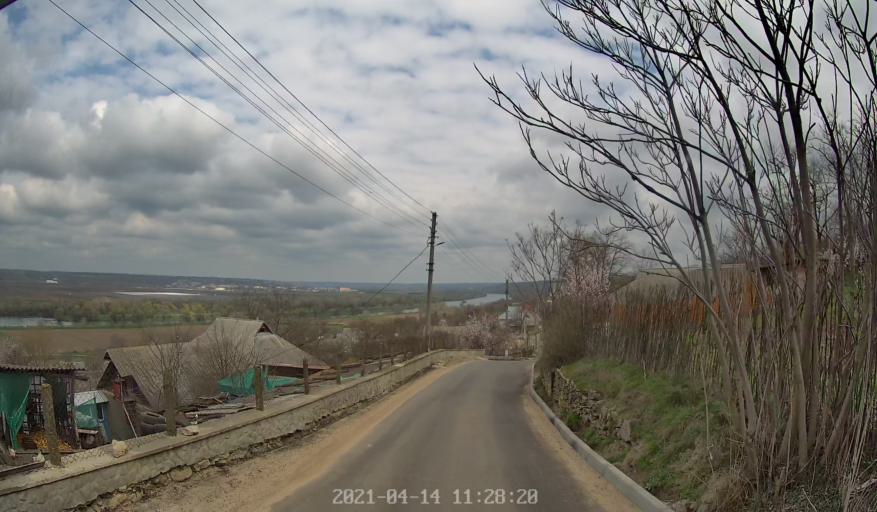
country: MD
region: Criuleni
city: Criuleni
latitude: 47.1772
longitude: 29.1644
